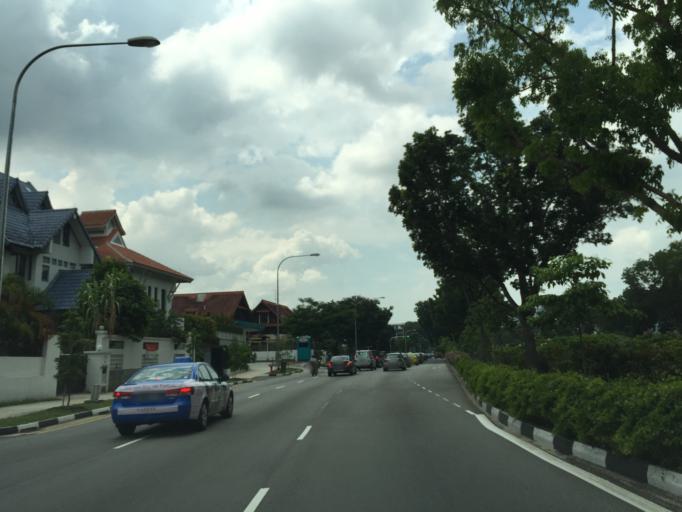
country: SG
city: Singapore
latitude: 1.3230
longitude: 103.8185
